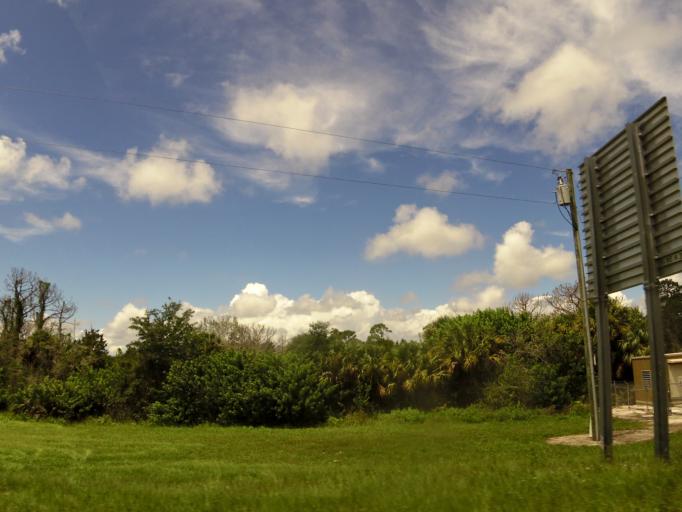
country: US
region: Florida
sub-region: Brevard County
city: Titusville
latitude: 28.6173
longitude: -80.8517
